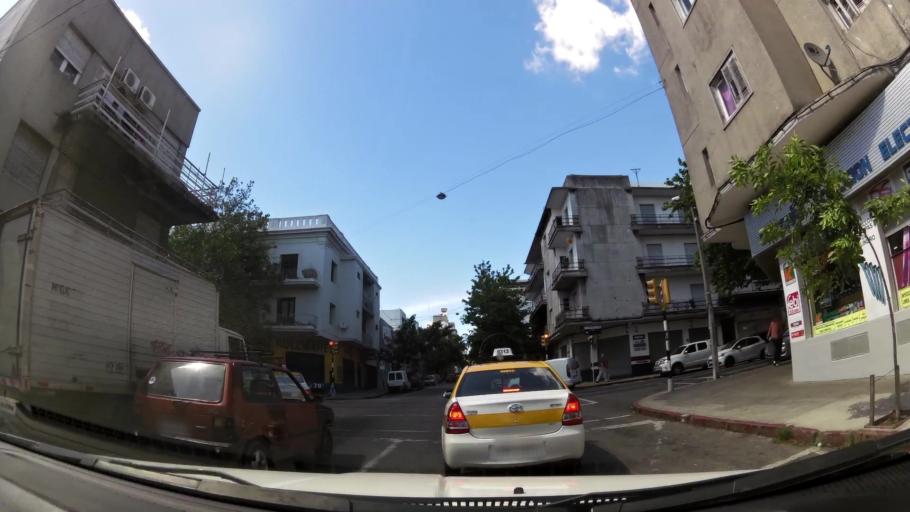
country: UY
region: Montevideo
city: Montevideo
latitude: -34.8999
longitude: -56.1886
